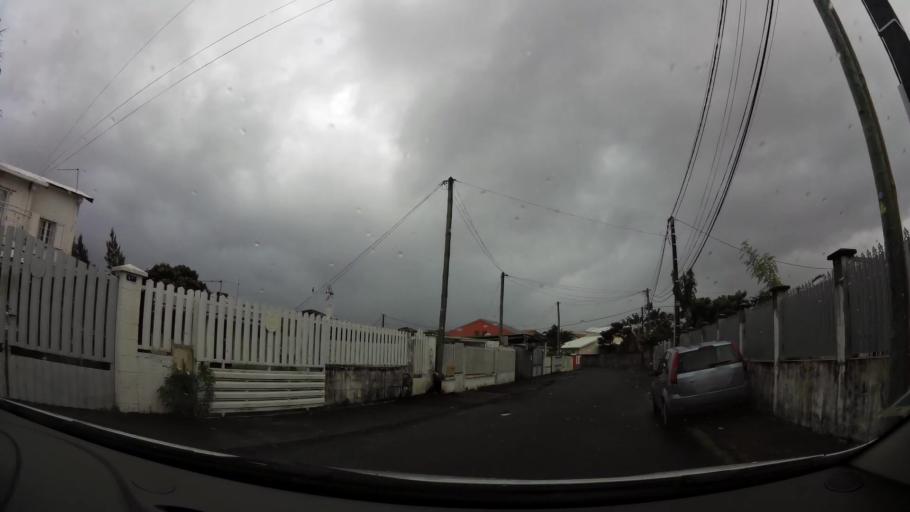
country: RE
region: Reunion
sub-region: Reunion
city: Saint-Andre
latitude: -20.9344
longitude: 55.6499
